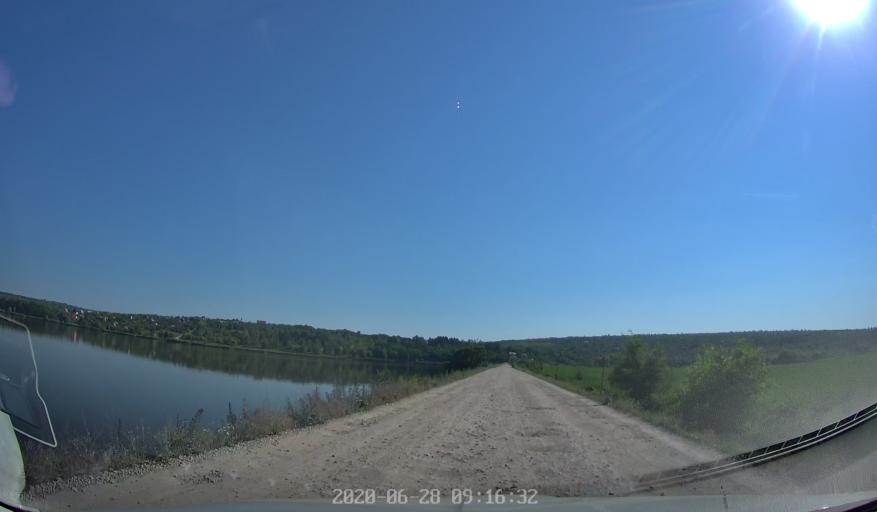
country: MD
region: Laloveni
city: Ialoveni
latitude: 46.9781
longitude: 28.7000
